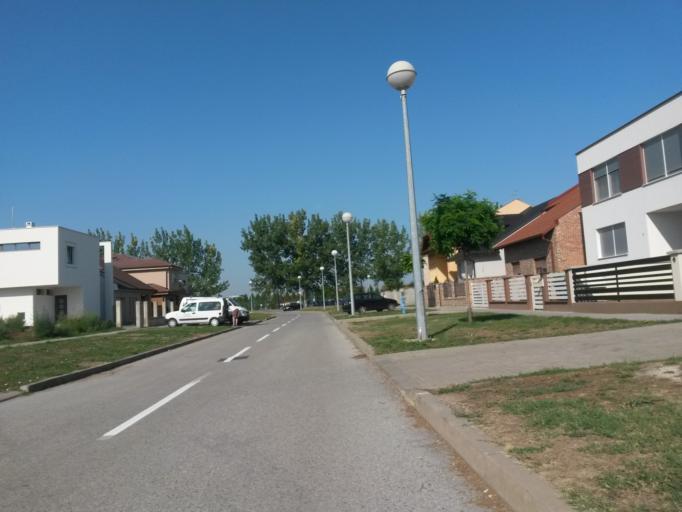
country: HR
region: Osjecko-Baranjska
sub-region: Grad Osijek
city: Osijek
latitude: 45.5418
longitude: 18.6987
